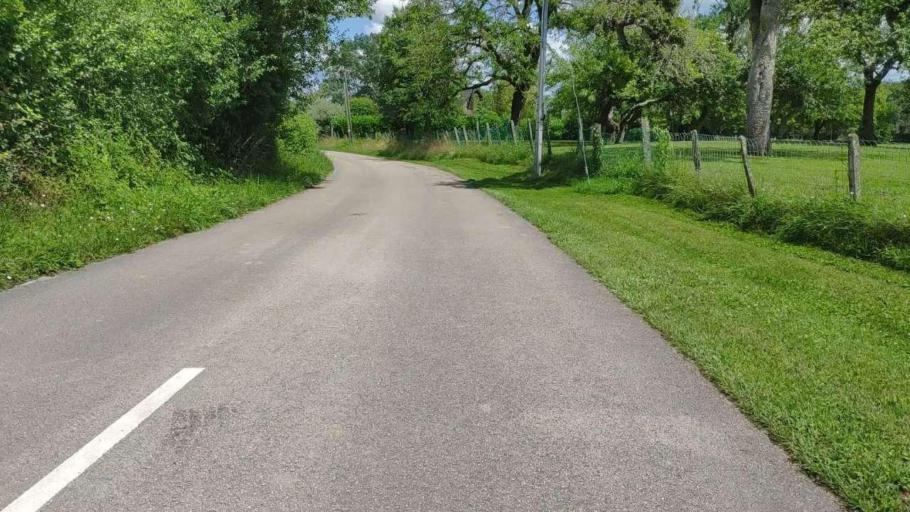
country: FR
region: Franche-Comte
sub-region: Departement du Jura
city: Bletterans
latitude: 46.8456
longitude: 5.4844
